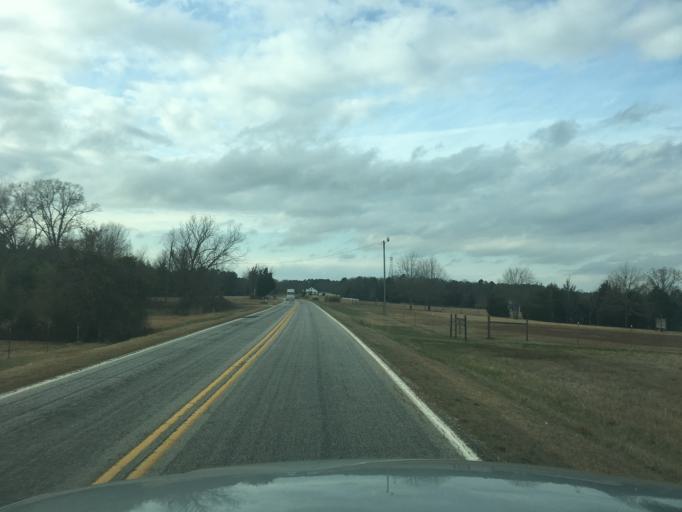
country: US
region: South Carolina
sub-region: Abbeville County
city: Due West
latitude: 34.3196
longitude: -82.4661
